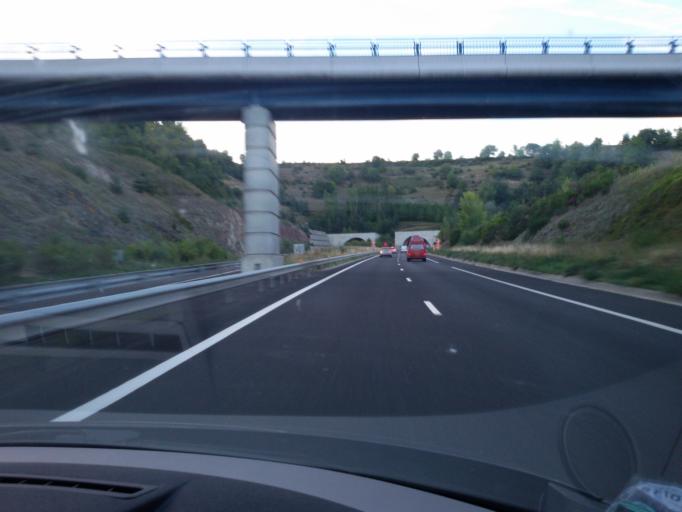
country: FR
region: Languedoc-Roussillon
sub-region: Departement de la Lozere
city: La Canourgue
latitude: 44.4788
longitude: 3.1983
